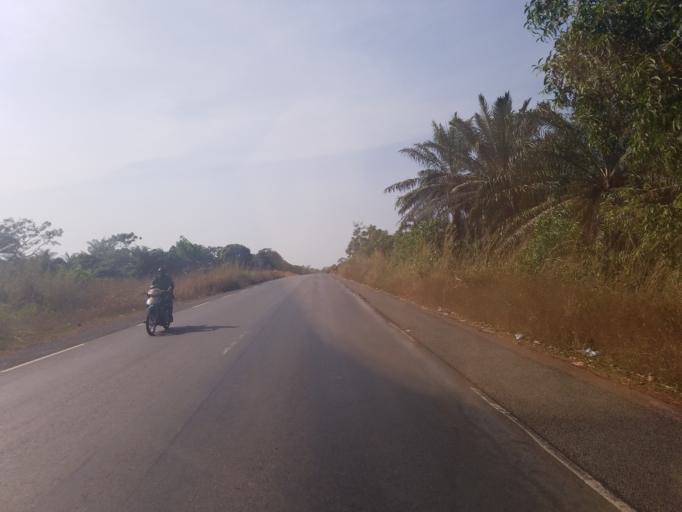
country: GN
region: Boke
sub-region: Boffa
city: Boffa
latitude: 10.1900
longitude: -14.0503
